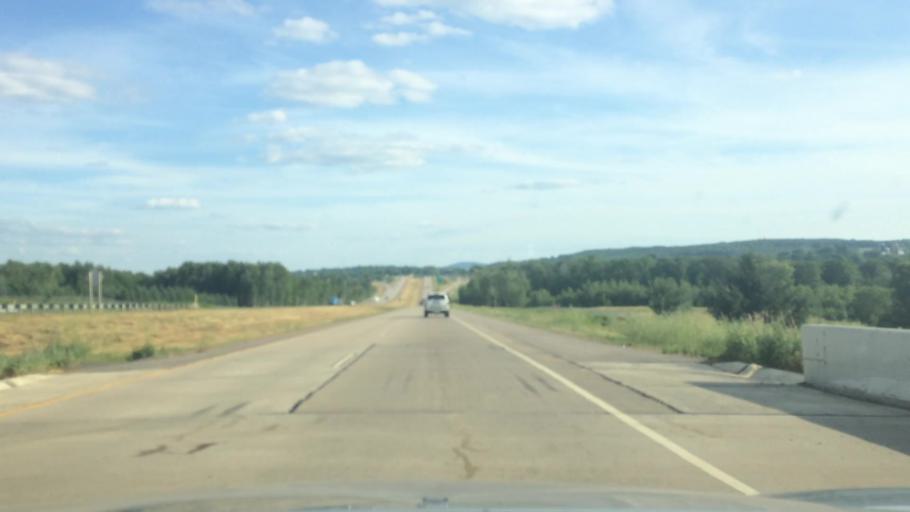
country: US
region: Wisconsin
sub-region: Marathon County
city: Wausau
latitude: 45.0026
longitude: -89.6586
